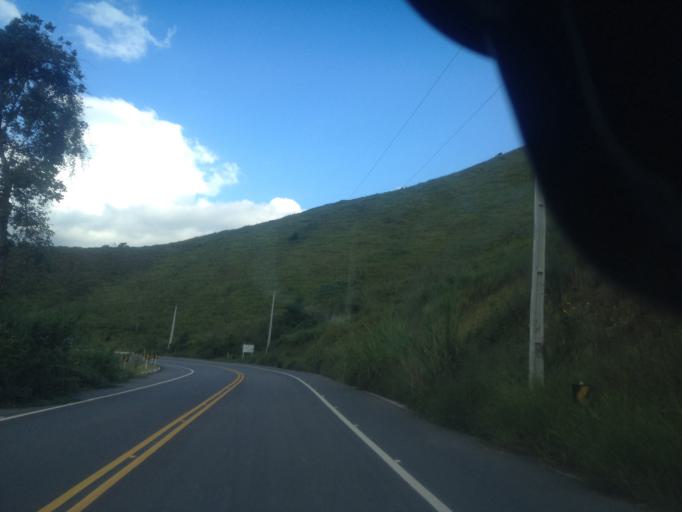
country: BR
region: Rio de Janeiro
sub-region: Quatis
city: Quatis
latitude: -22.2700
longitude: -44.2606
